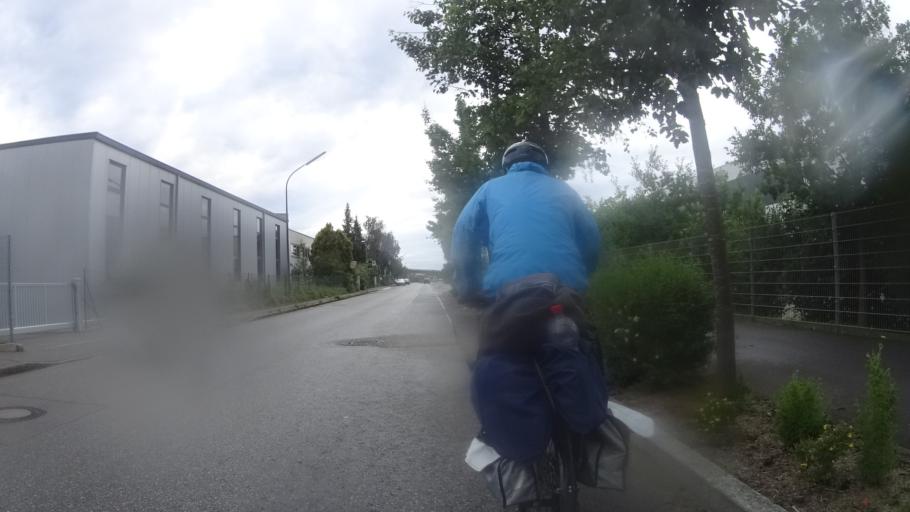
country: DE
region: Bavaria
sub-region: Upper Bavaria
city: Maisach
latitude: 48.2142
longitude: 11.2855
